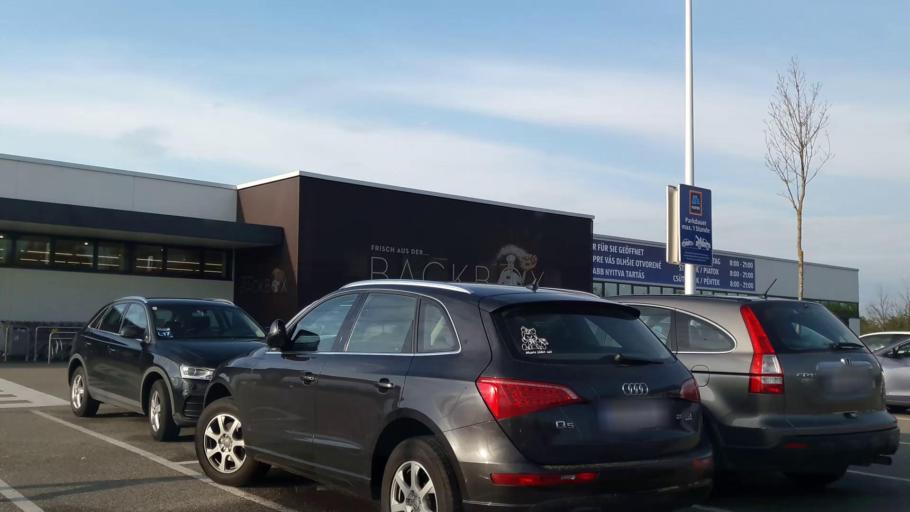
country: AT
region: Burgenland
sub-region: Politischer Bezirk Neusiedl am See
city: Parndorf
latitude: 47.9778
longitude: 16.8536
